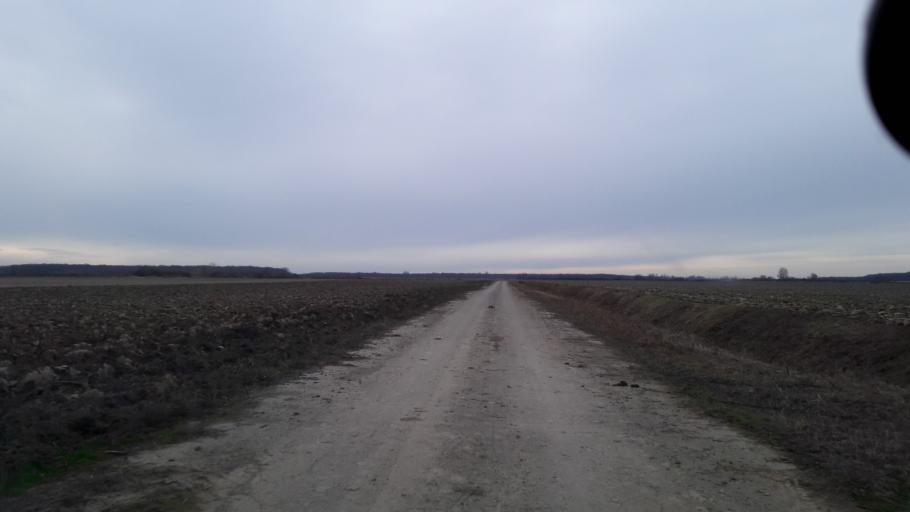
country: HR
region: Osjecko-Baranjska
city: Vladislavci
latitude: 45.4293
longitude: 18.5739
